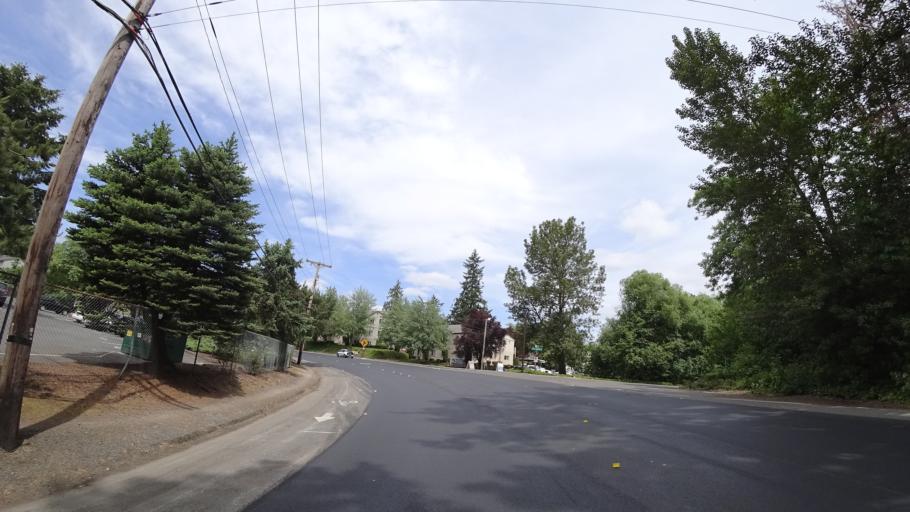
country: US
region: Oregon
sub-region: Washington County
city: Metzger
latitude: 45.4495
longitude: -122.7645
